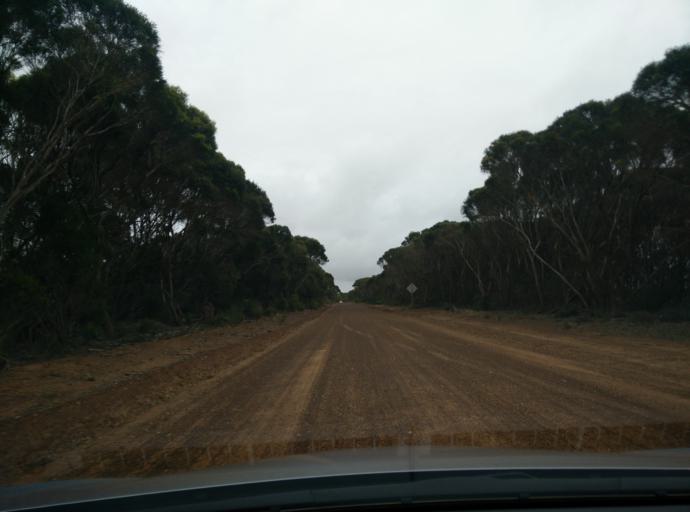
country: AU
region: South Australia
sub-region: Kangaroo Island
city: Kingscote
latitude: -35.8524
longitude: 137.4821
